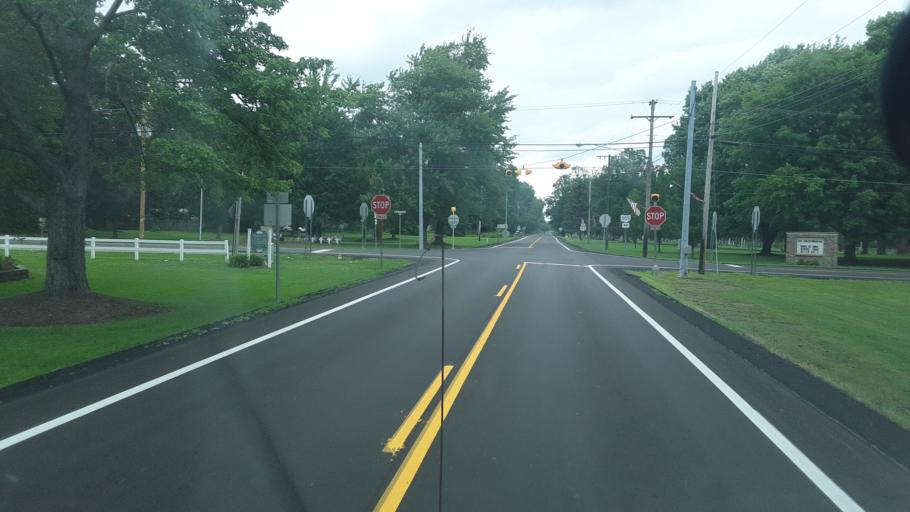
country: US
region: Ohio
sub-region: Trumbull County
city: Cortland
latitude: 41.3107
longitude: -80.6557
